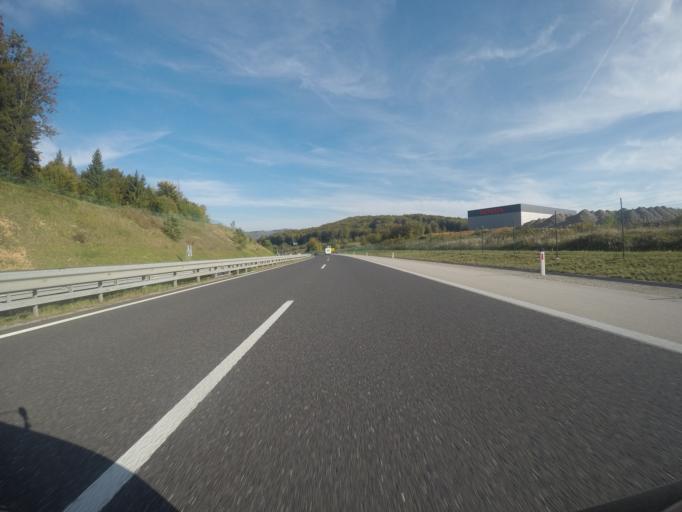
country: SI
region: Mirna Pec
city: Mirna Pec
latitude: 45.8739
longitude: 15.0921
